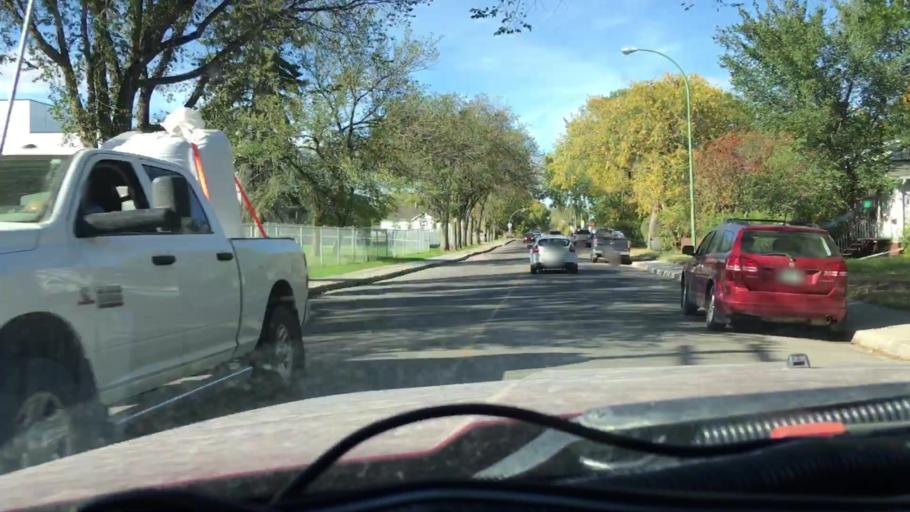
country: CA
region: Saskatchewan
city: Regina
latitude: 50.4568
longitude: -104.6312
